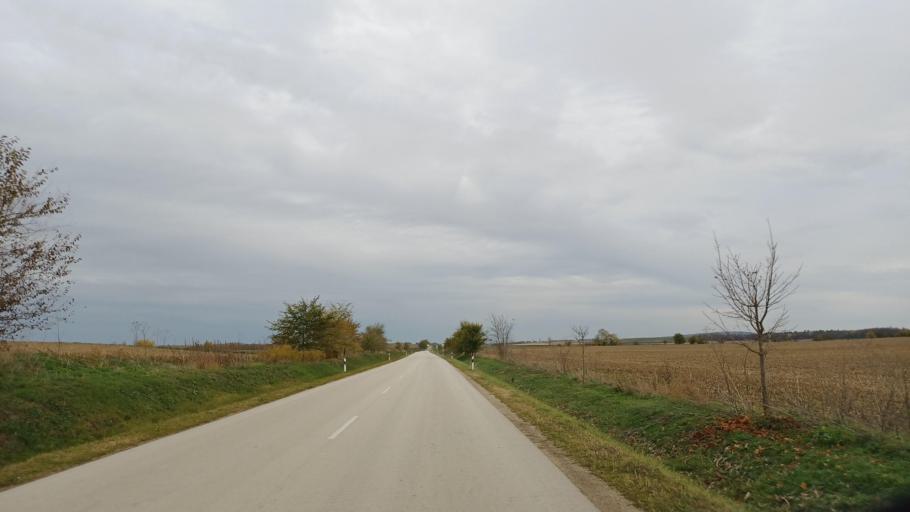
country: HU
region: Tolna
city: Nagydorog
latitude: 46.6669
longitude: 18.6036
